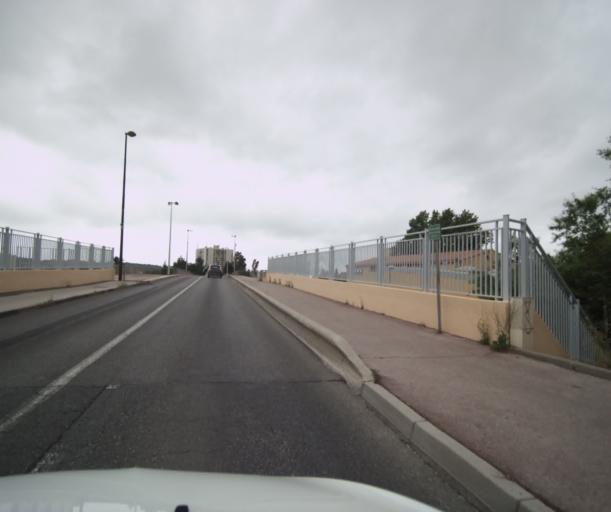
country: FR
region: Provence-Alpes-Cote d'Azur
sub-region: Departement du Var
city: La Valette-du-Var
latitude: 43.1351
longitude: 5.9873
